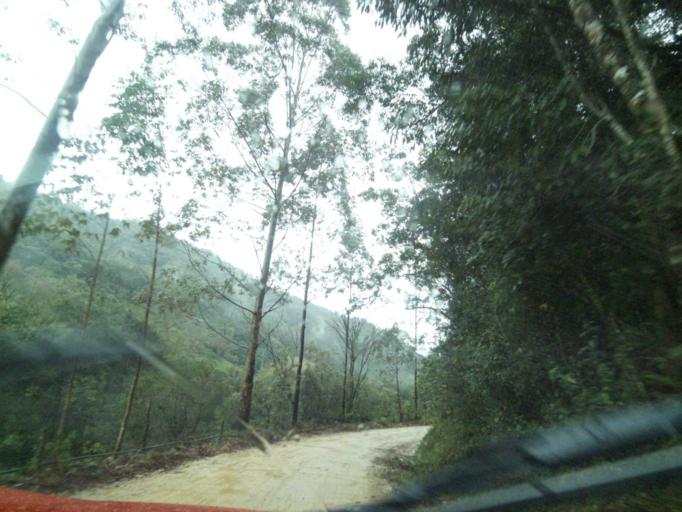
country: BR
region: Santa Catarina
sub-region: Anitapolis
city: Anitapolis
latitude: -27.9172
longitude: -49.1927
